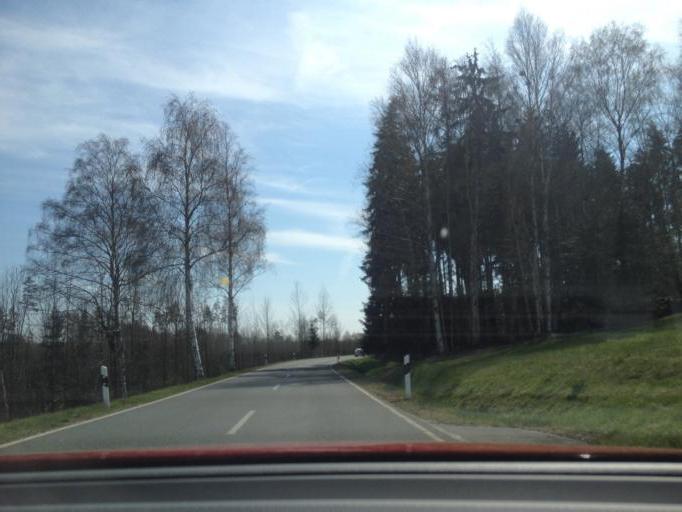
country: DE
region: Bavaria
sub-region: Upper Franconia
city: Weissenstadt
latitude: 50.0911
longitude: 11.9084
